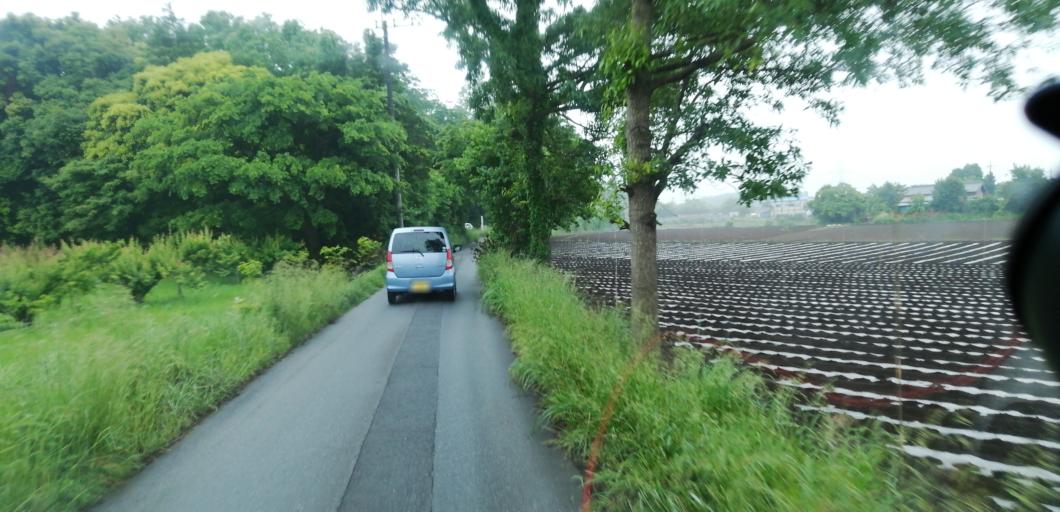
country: JP
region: Chiba
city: Ichihara
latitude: 35.4855
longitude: 140.1477
